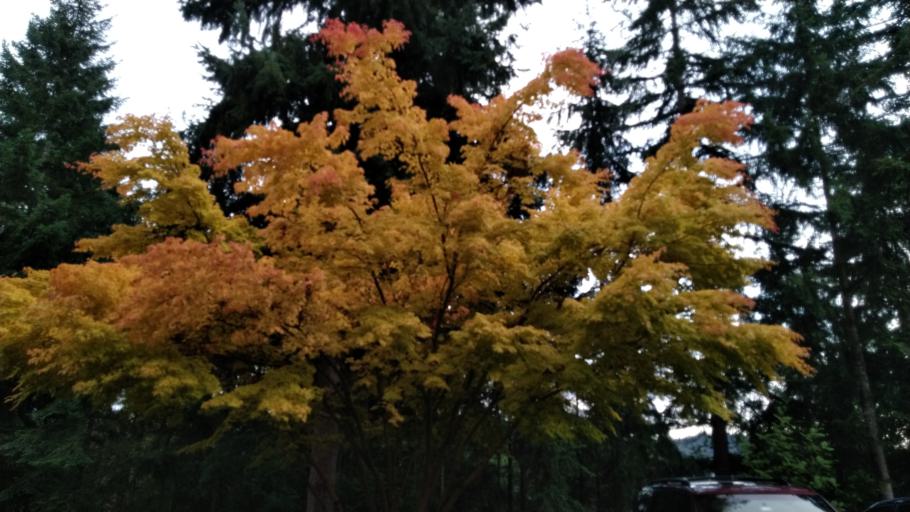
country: US
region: Washington
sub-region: King County
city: Eastgate
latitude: 47.5836
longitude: -122.1409
